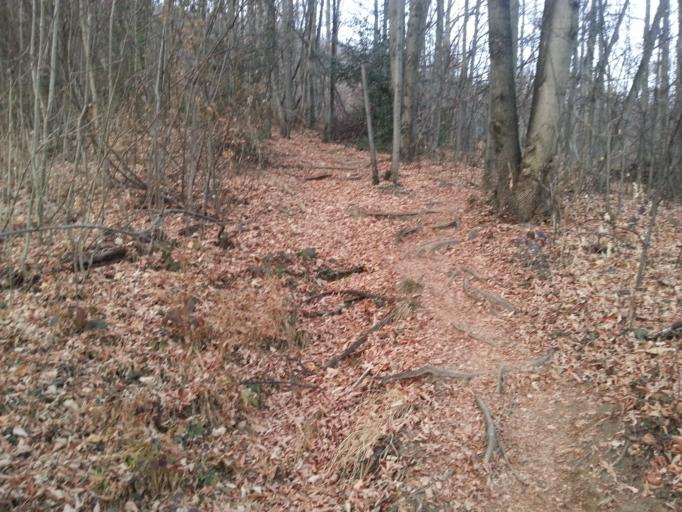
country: CH
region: Ticino
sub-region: Lugano District
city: Pura
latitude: 46.0268
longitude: 8.8517
